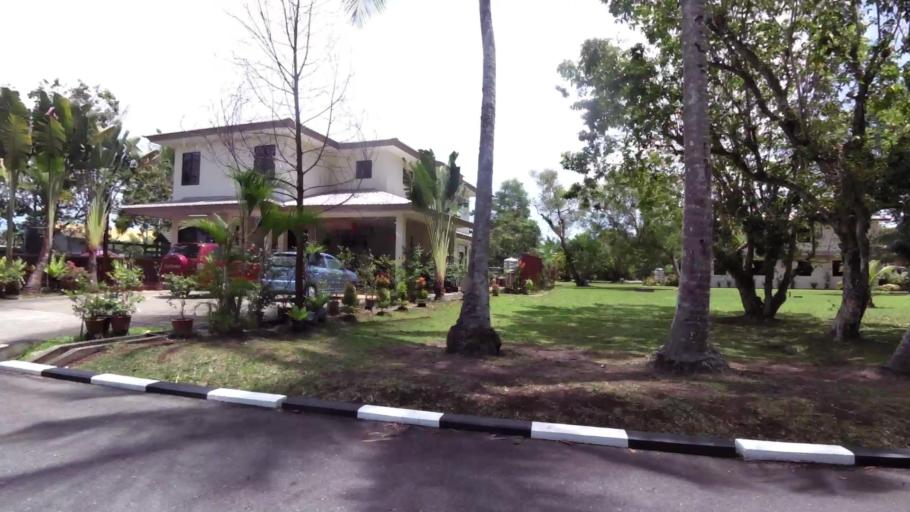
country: BN
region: Belait
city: Kuala Belait
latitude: 4.5946
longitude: 114.2538
